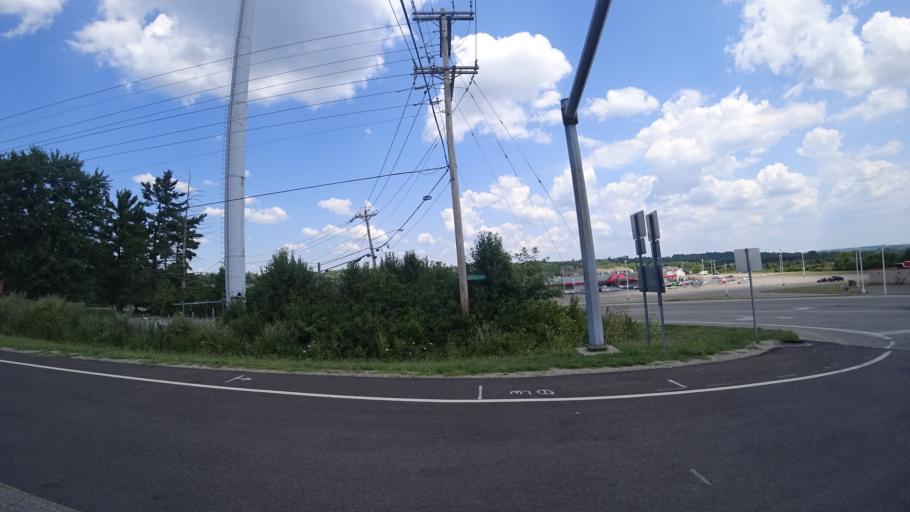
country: US
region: Ohio
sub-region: Butler County
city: Hamilton
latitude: 39.4299
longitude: -84.6000
